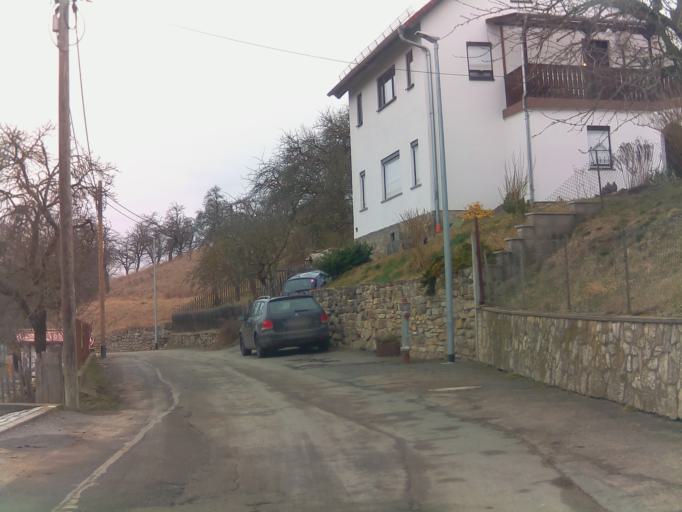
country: DE
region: Thuringia
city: Bad Blankenburg
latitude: 50.6998
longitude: 11.2478
